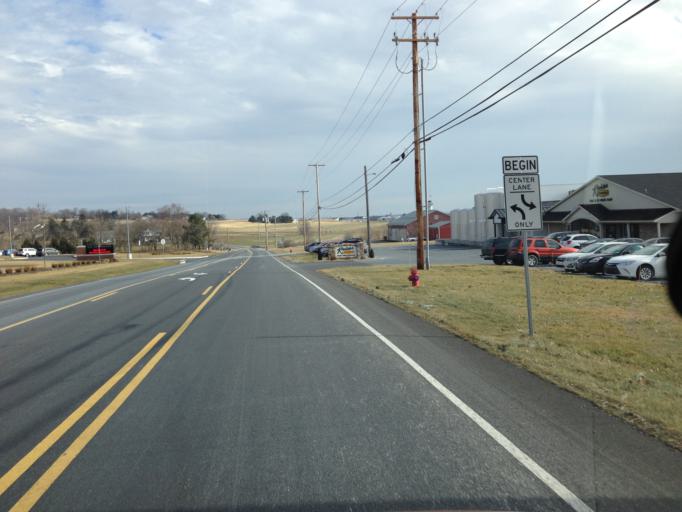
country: US
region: Pennsylvania
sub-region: Lancaster County
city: Manheim
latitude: 40.1733
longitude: -76.3734
